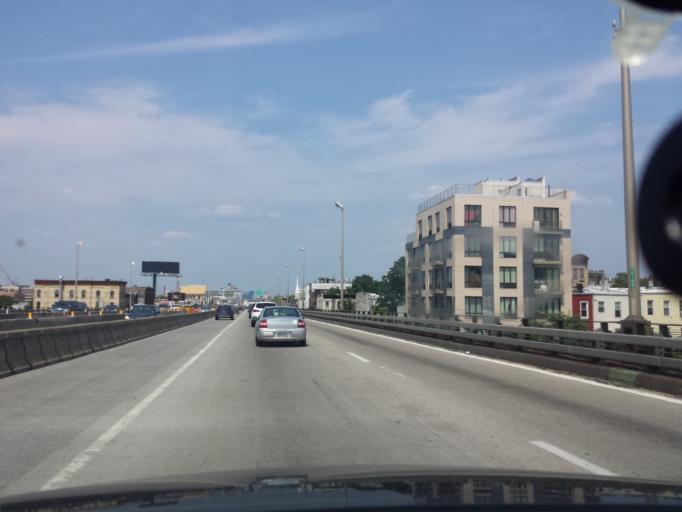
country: US
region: New York
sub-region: Kings County
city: Bensonhurst
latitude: 40.6460
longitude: -74.0163
